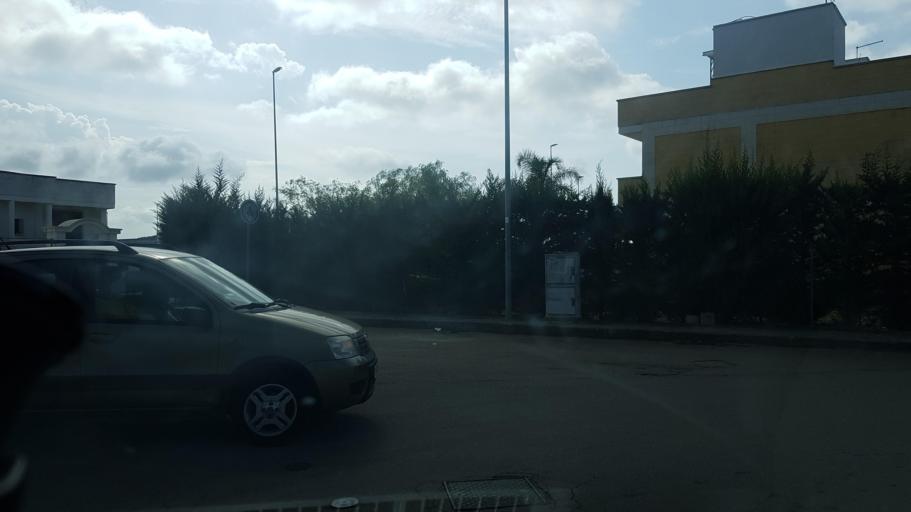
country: IT
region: Apulia
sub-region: Provincia di Brindisi
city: San Donaci
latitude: 40.4482
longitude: 17.9305
